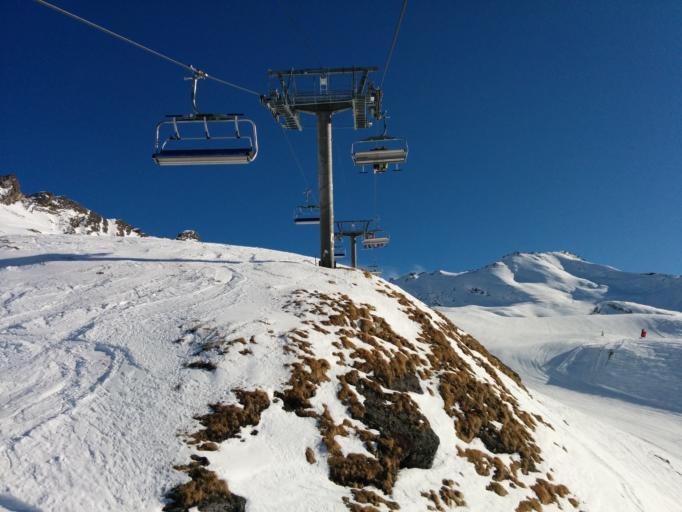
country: FR
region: Rhone-Alpes
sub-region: Departement de la Savoie
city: Val-d'Isere
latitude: 45.4259
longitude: 7.0049
